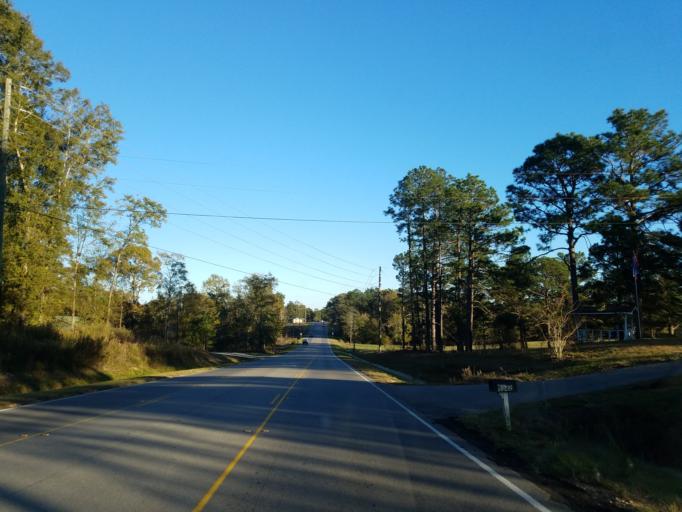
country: US
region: Mississippi
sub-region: Lamar County
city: Arnold Line
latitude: 31.3379
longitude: -89.3955
